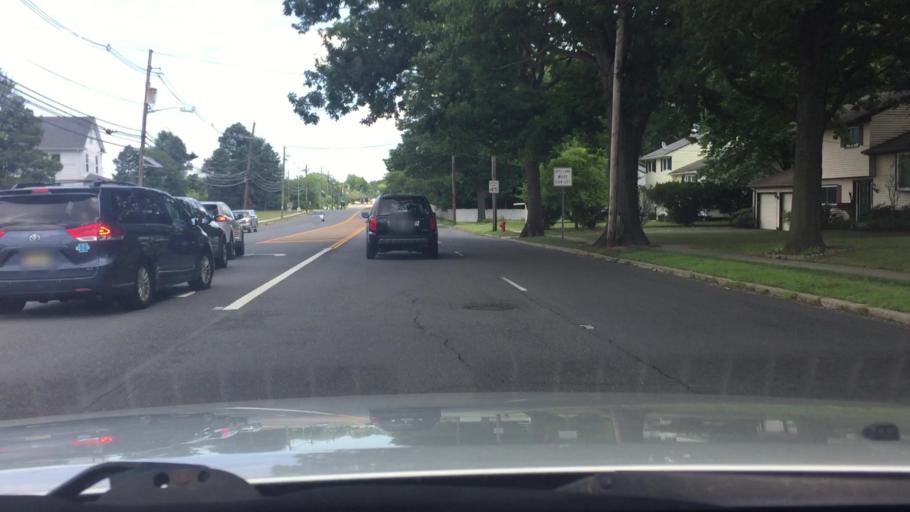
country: US
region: New Jersey
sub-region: Middlesex County
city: Old Bridge
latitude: 40.4201
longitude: -74.3841
